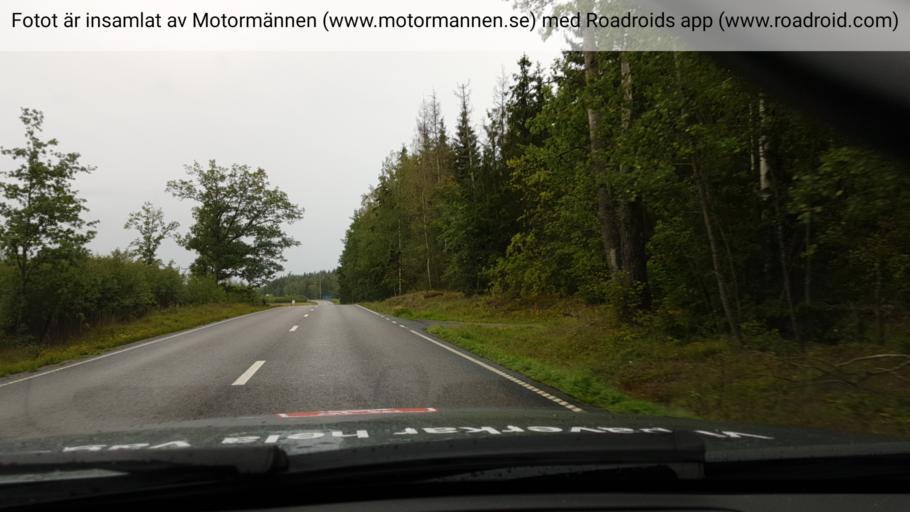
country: SE
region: Soedermanland
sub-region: Eskilstuna Kommun
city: Eskilstuna
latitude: 59.3253
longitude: 16.5302
